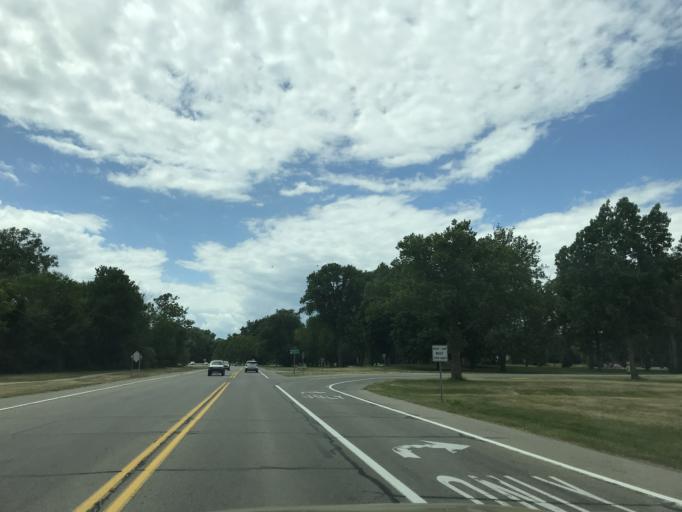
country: US
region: Michigan
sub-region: Wayne County
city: Dearborn Heights
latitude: 42.3467
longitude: -83.2748
